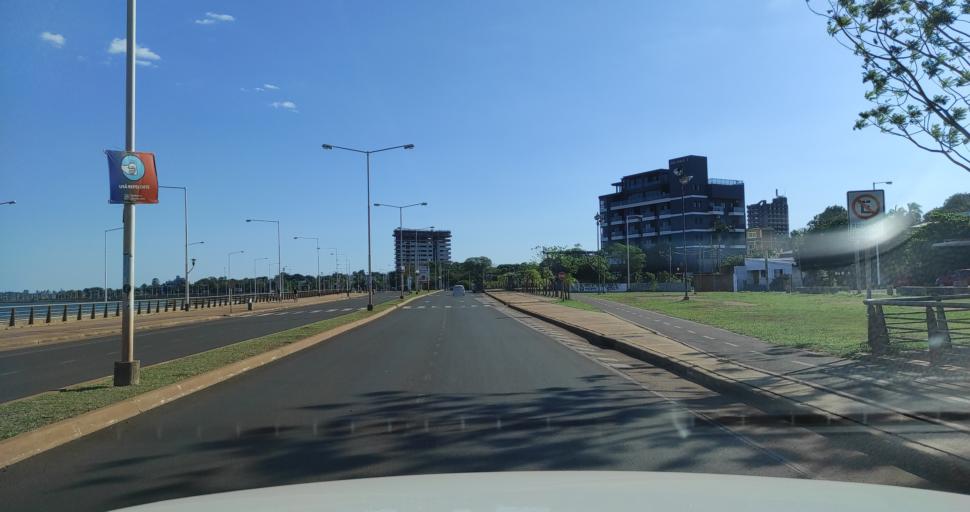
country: AR
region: Misiones
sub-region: Departamento de Capital
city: Posadas
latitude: -27.3907
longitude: -55.8887
